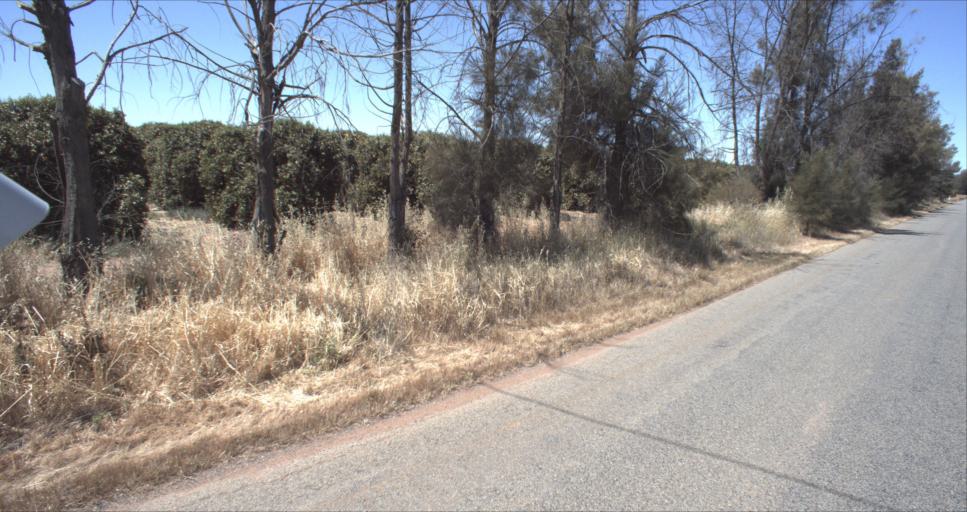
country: AU
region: New South Wales
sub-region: Leeton
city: Leeton
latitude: -34.5353
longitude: 146.3570
